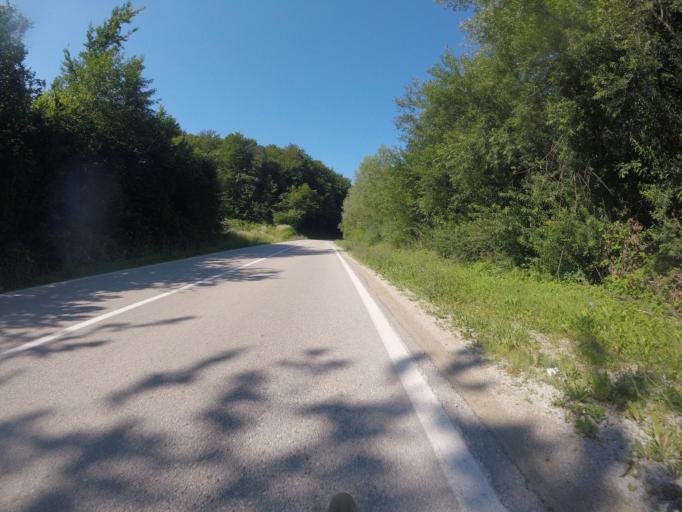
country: HR
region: Zagrebacka
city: Bregana
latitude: 45.8343
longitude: 15.6564
